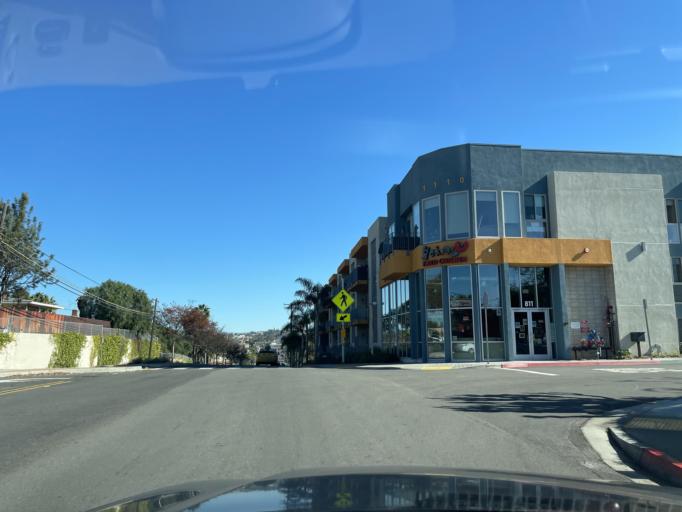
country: US
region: California
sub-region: San Diego County
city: National City
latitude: 32.6789
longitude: -117.0959
